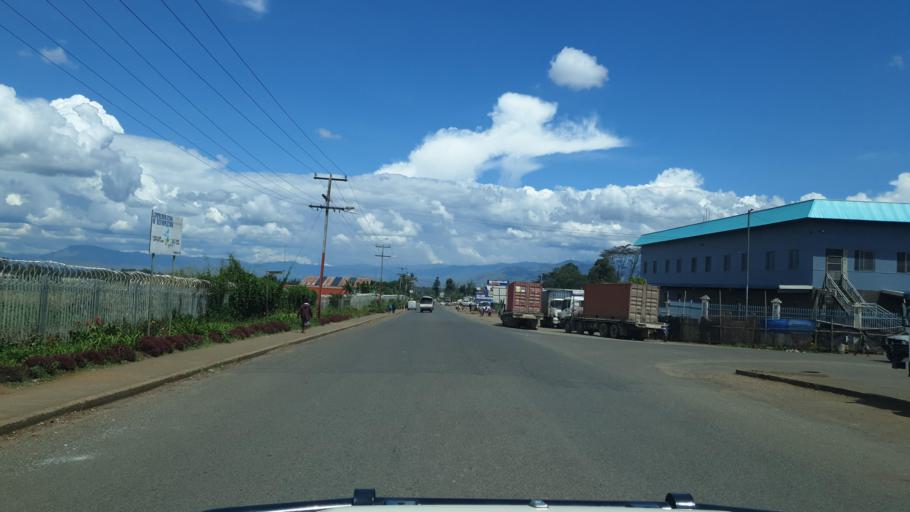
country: PG
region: Eastern Highlands
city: Goroka
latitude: -6.0824
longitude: 145.3898
